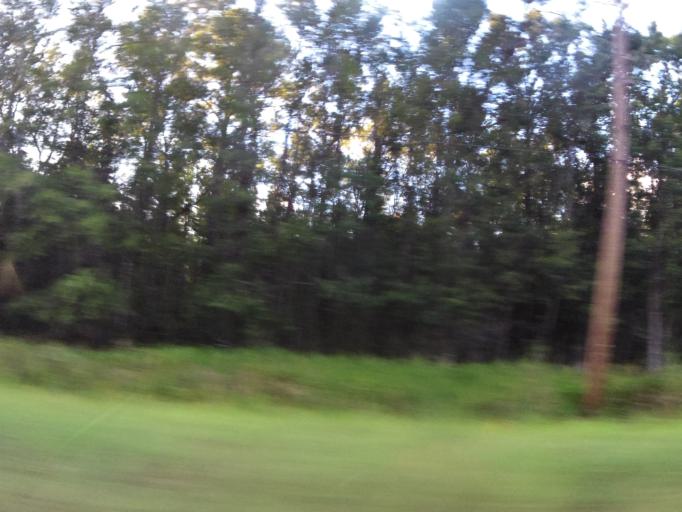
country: US
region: Georgia
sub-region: Camden County
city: Woodbine
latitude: 31.0986
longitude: -81.7218
